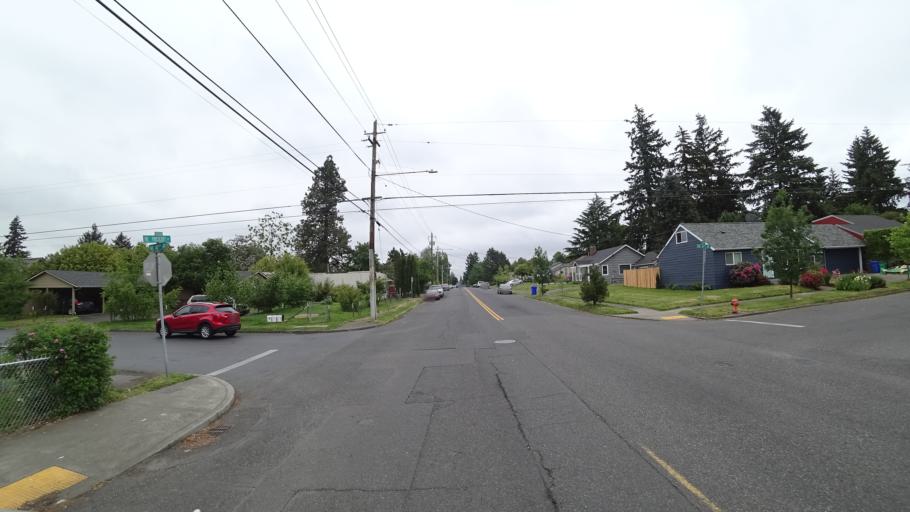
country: US
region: Oregon
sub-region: Multnomah County
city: Portland
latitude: 45.5555
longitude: -122.6150
